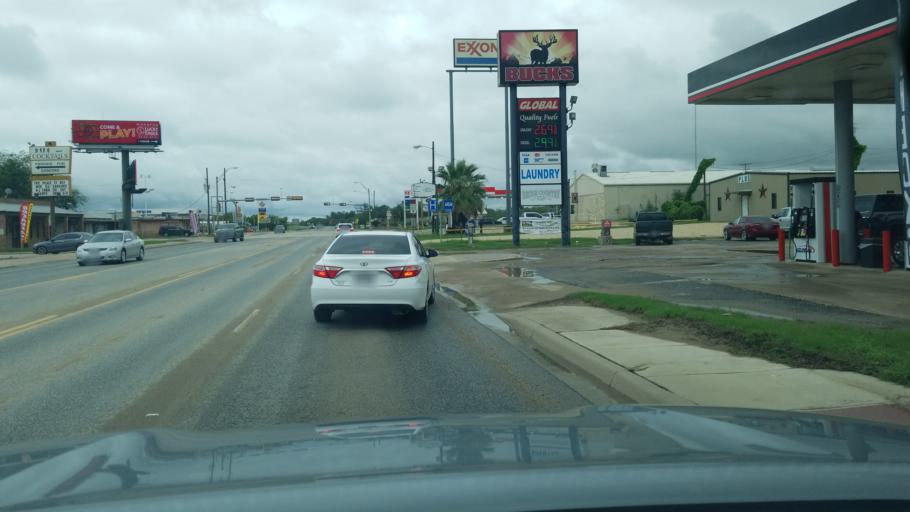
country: US
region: Texas
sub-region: Dimmit County
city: Carrizo Springs
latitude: 28.5223
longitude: -99.8569
